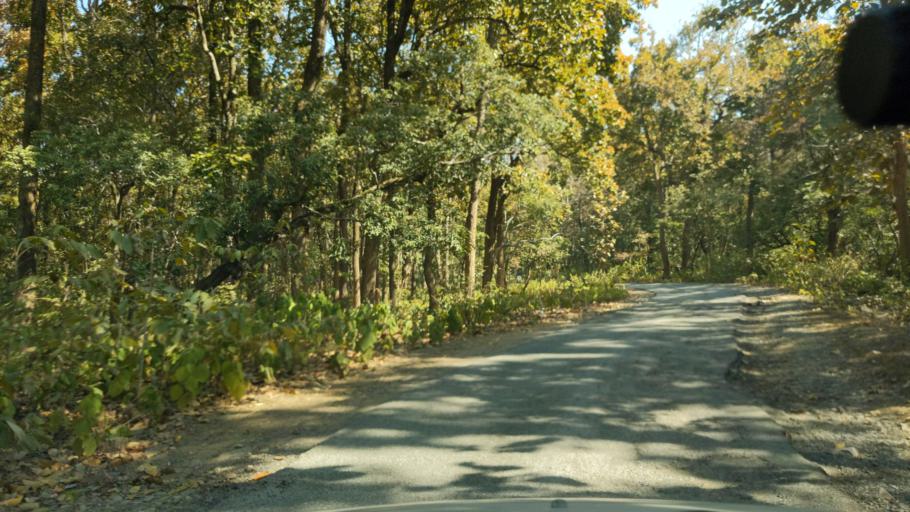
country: IN
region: Uttarakhand
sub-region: Naini Tal
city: Ramnagar
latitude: 29.4602
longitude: 79.2286
